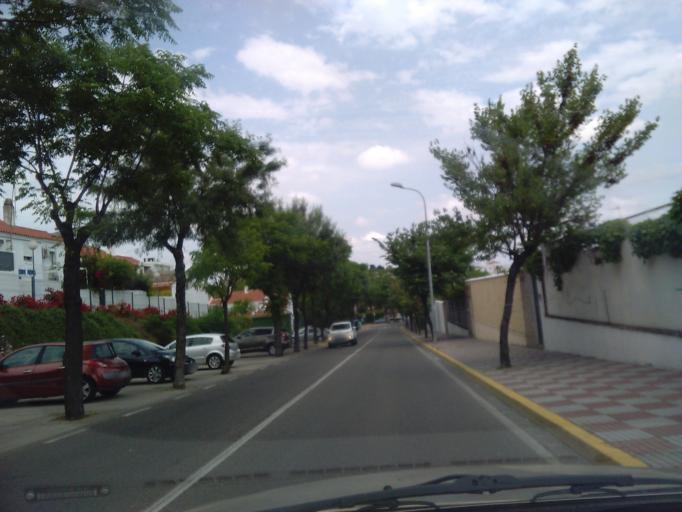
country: ES
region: Andalusia
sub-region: Provincia de Sevilla
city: Tomares
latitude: 37.3702
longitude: -6.0406
